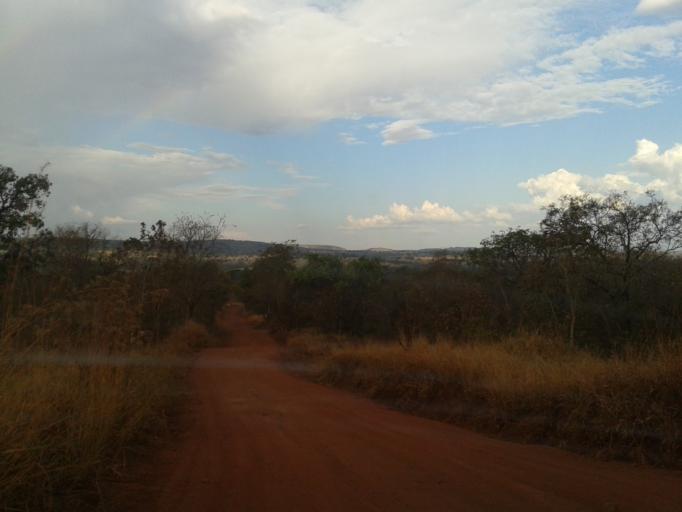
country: BR
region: Minas Gerais
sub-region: Santa Vitoria
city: Santa Vitoria
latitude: -19.1785
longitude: -49.8546
